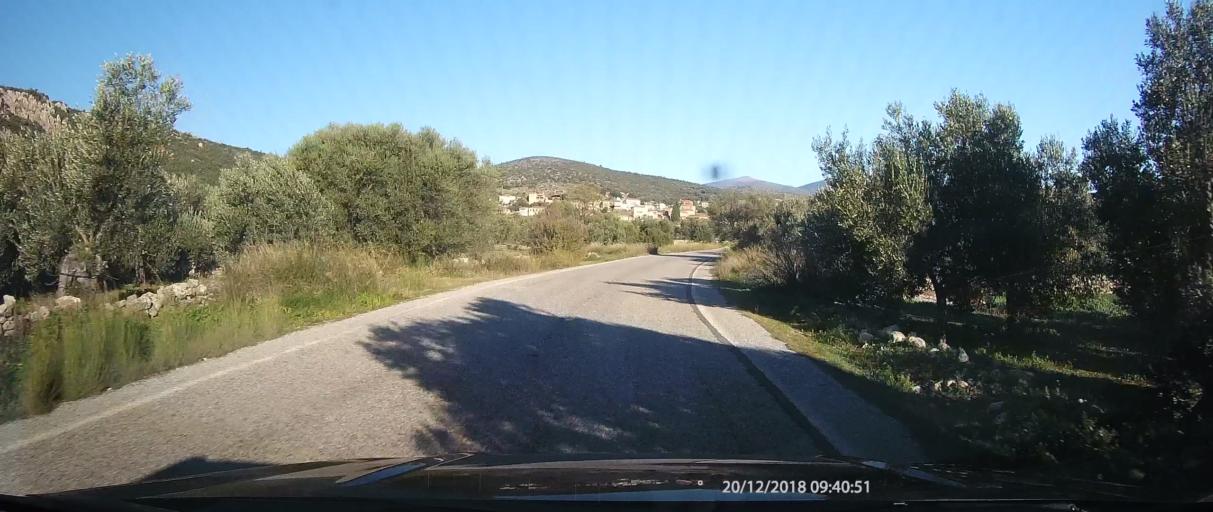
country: GR
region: Peloponnese
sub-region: Nomos Lakonias
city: Yerakion
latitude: 36.9484
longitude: 22.7665
